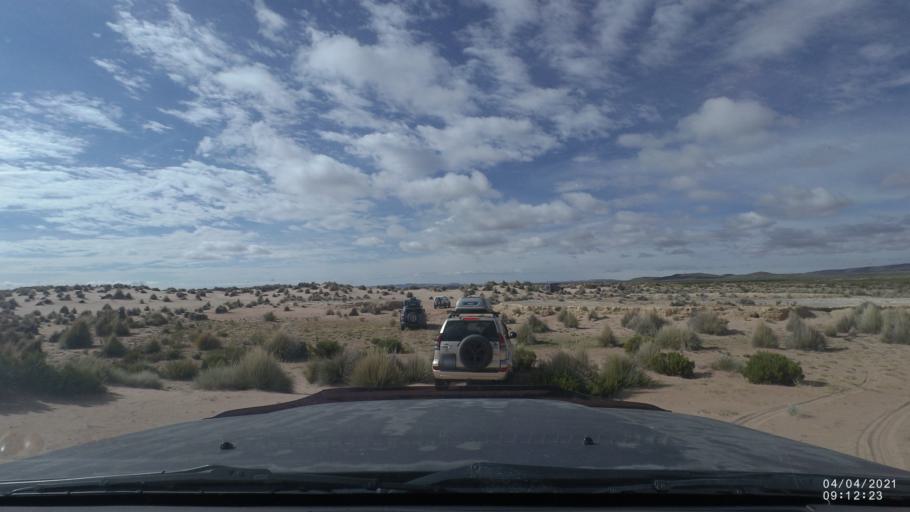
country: BO
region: Oruro
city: Poopo
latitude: -18.7143
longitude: -67.4819
